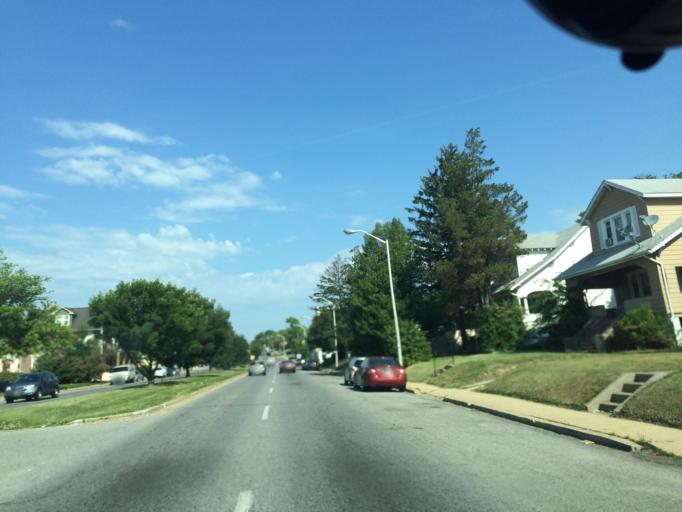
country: US
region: Maryland
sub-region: Baltimore County
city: Parkville
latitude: 39.3627
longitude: -76.5498
